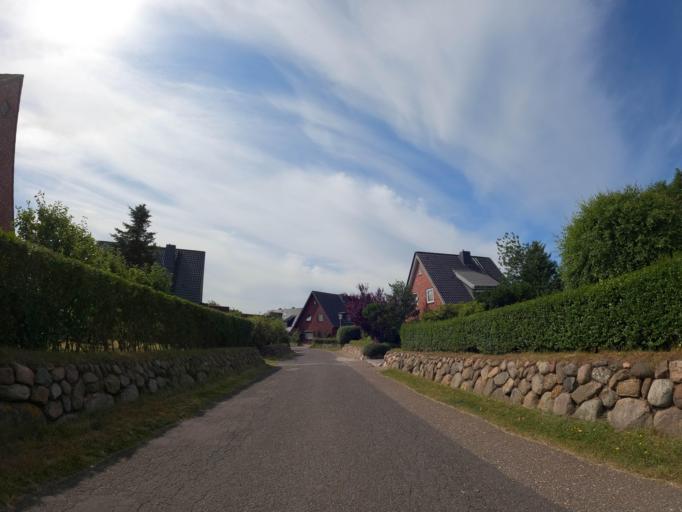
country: DE
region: Schleswig-Holstein
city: Westerland
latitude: 54.9234
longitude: 8.3207
